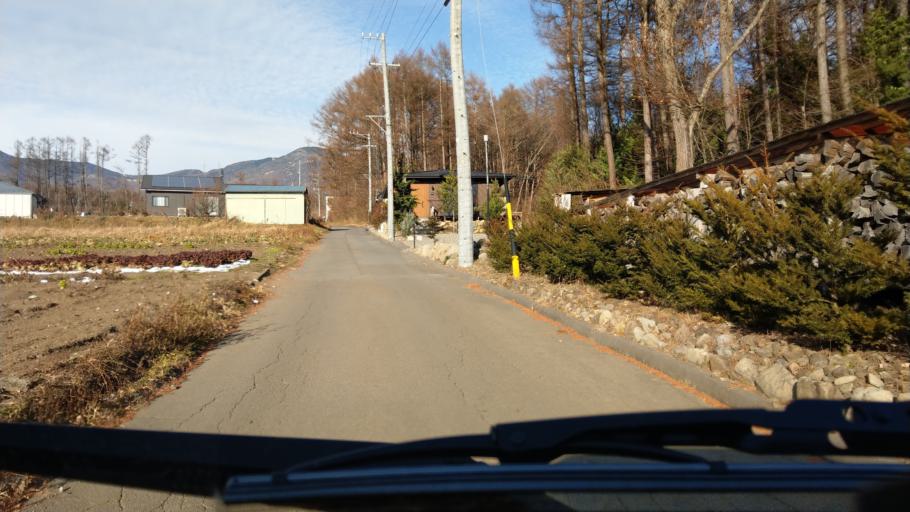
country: JP
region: Nagano
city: Komoro
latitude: 36.3415
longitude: 138.4615
